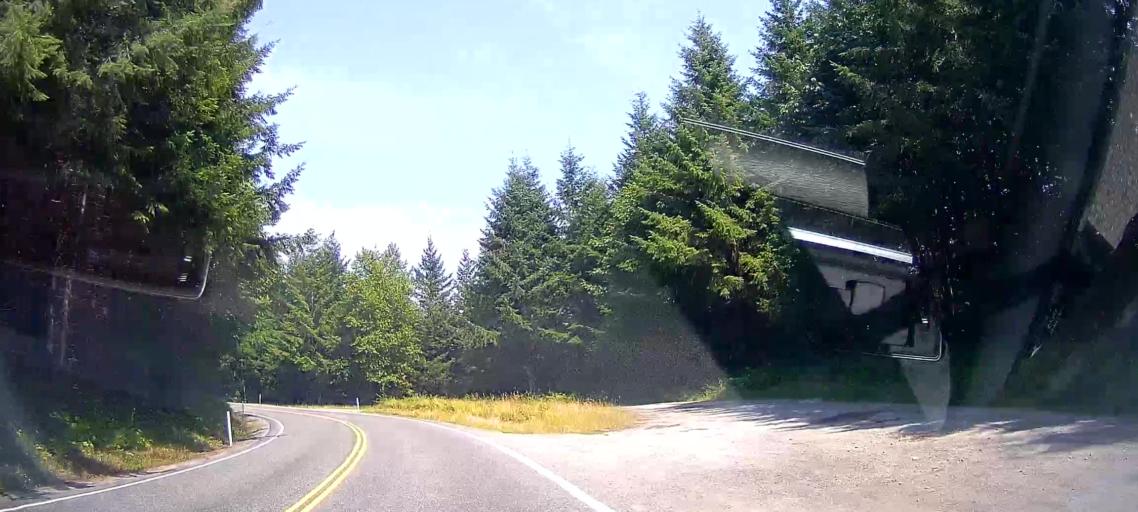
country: US
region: Washington
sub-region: Snohomish County
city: Bryant
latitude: 48.3353
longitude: -122.1257
